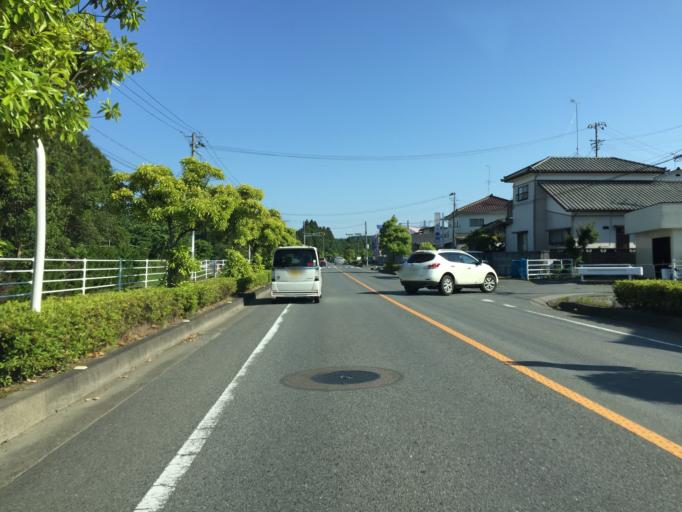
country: JP
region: Ibaraki
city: Kitaibaraki
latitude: 36.8964
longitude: 140.7673
